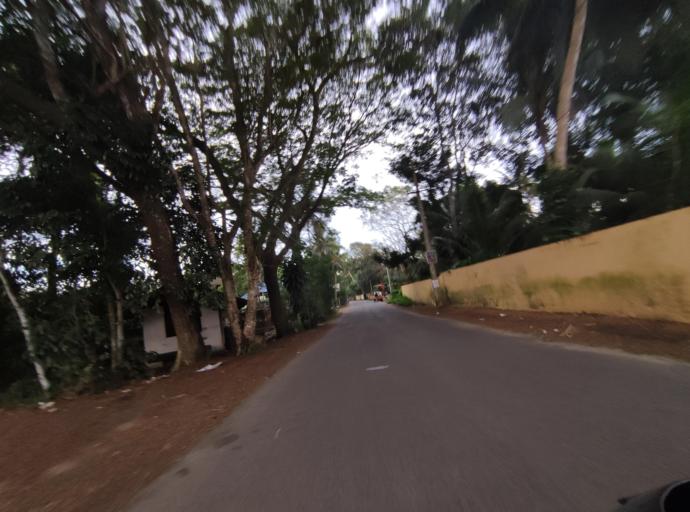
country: IN
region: Kerala
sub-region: Alappuzha
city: Shertallai
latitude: 9.6727
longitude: 76.3347
